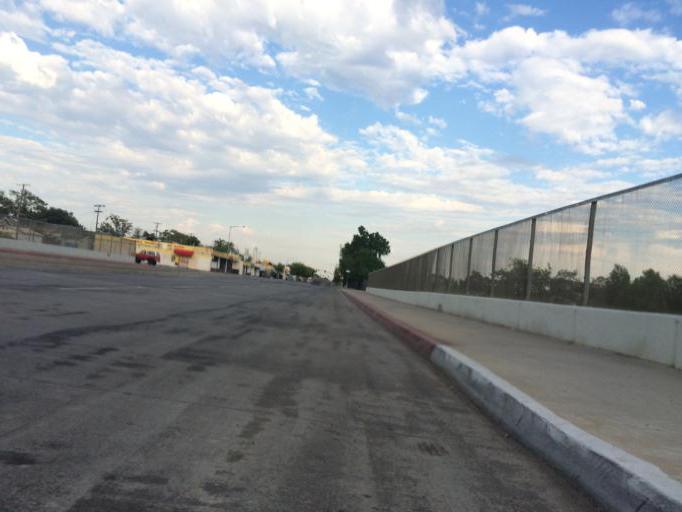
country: US
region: California
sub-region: Fresno County
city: Fresno
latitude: 36.7505
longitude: -119.7758
